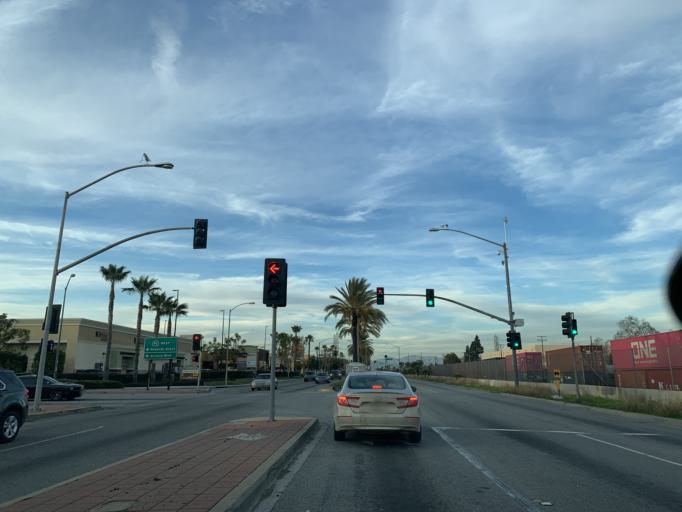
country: US
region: California
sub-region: Los Angeles County
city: Compton
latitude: 33.8760
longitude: -118.2173
